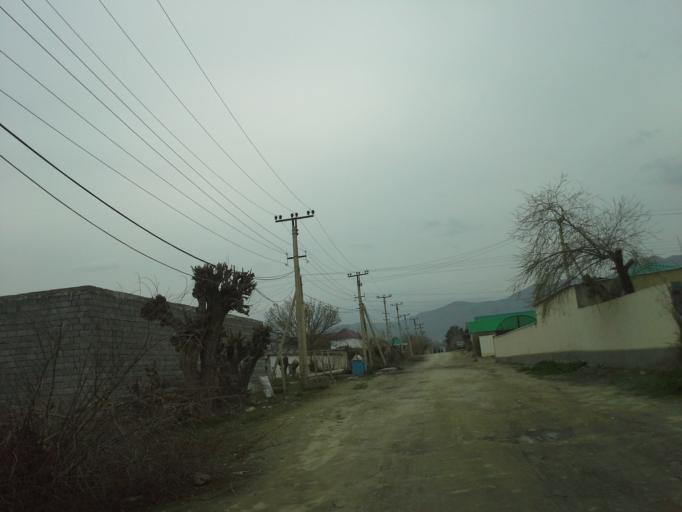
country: TM
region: Ahal
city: Abadan
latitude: 37.9716
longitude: 58.2208
